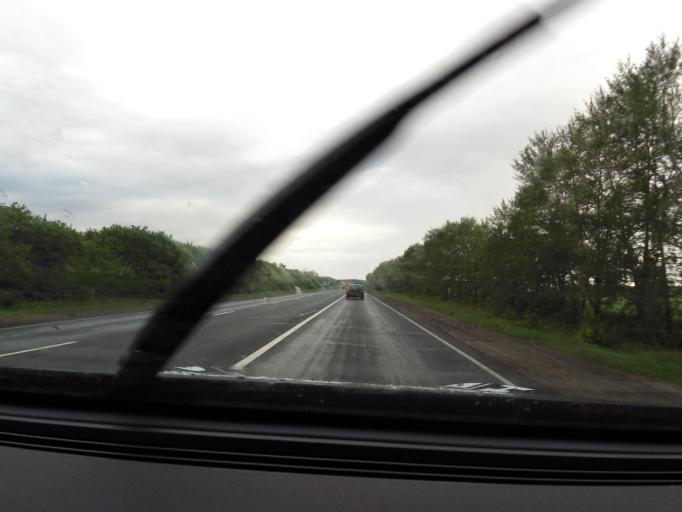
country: RU
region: Chuvashia
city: Yantikovo
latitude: 55.8003
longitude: 47.8656
